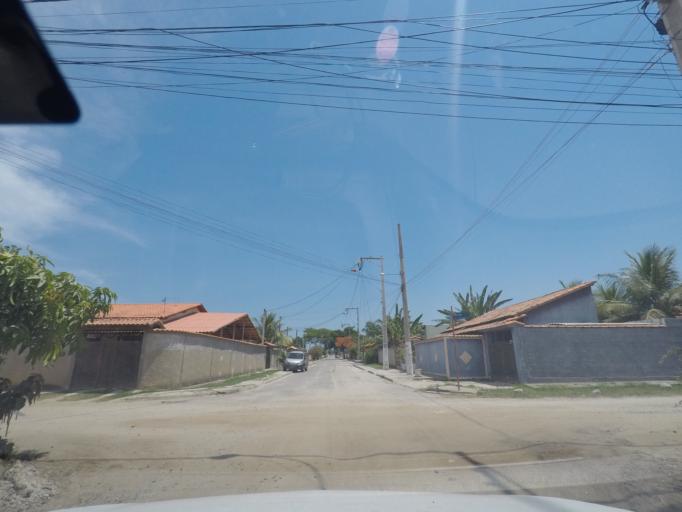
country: BR
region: Rio de Janeiro
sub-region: Niteroi
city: Niteroi
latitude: -22.9595
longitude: -42.9694
